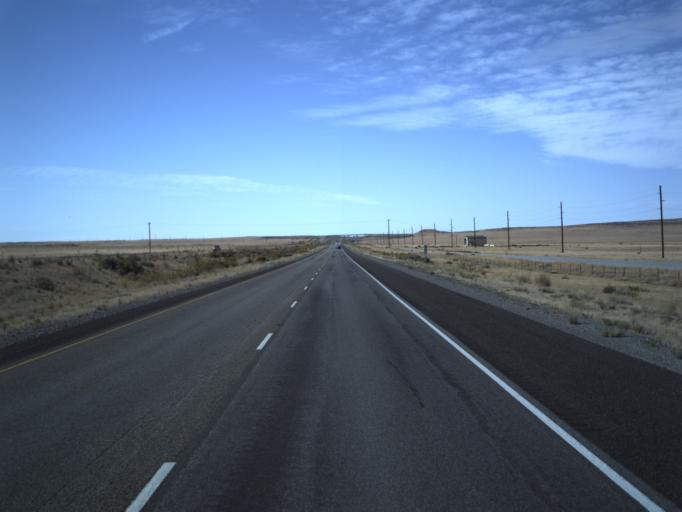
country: US
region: Utah
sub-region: Tooele County
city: Grantsville
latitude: 40.7877
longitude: -112.9592
